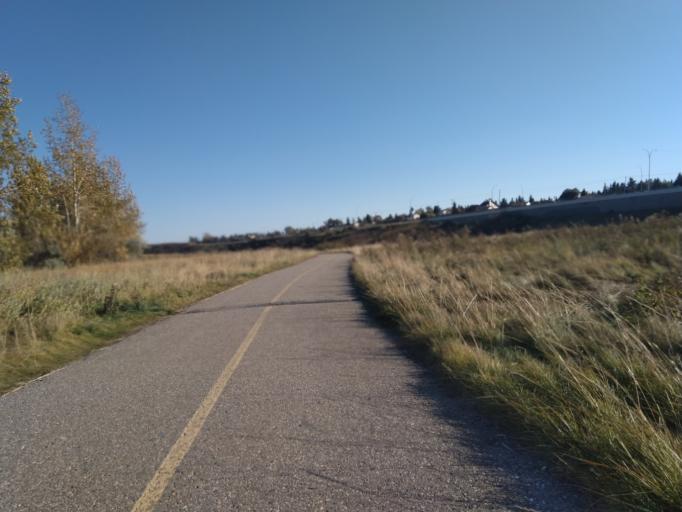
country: CA
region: Alberta
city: Calgary
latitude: 51.1352
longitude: -114.0688
